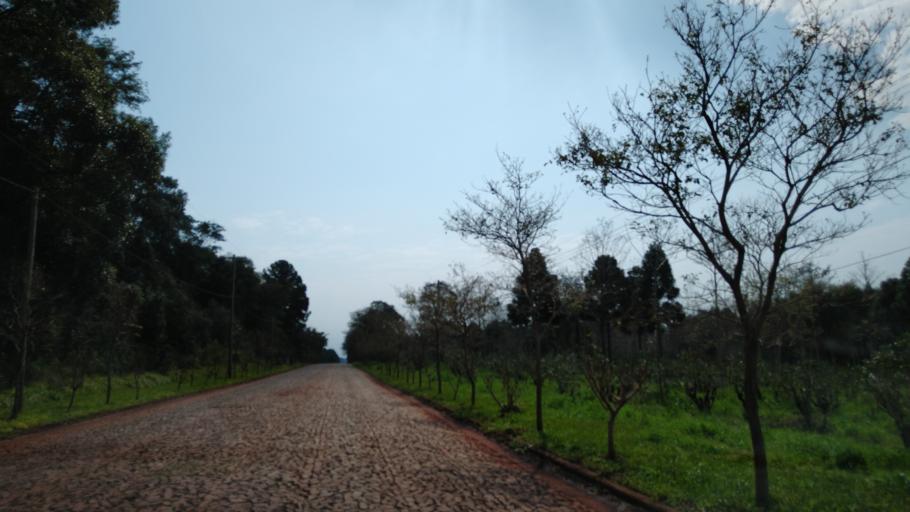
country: AR
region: Misiones
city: Capiovi
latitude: -26.9559
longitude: -55.0558
